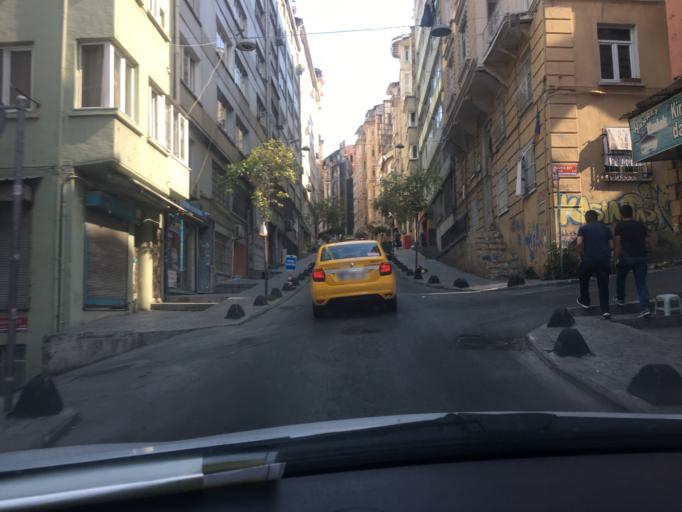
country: TR
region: Istanbul
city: Eminoenue
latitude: 41.0374
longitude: 28.9749
